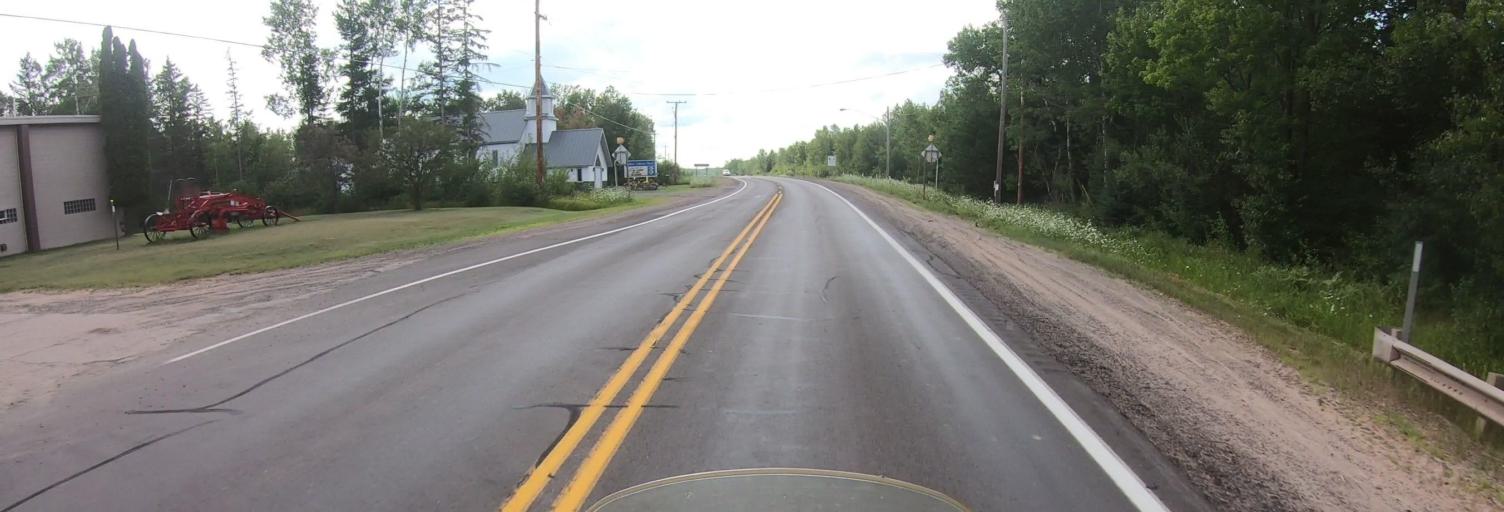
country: US
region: Michigan
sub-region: Ontonagon County
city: Ontonagon
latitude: 46.5349
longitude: -89.1837
